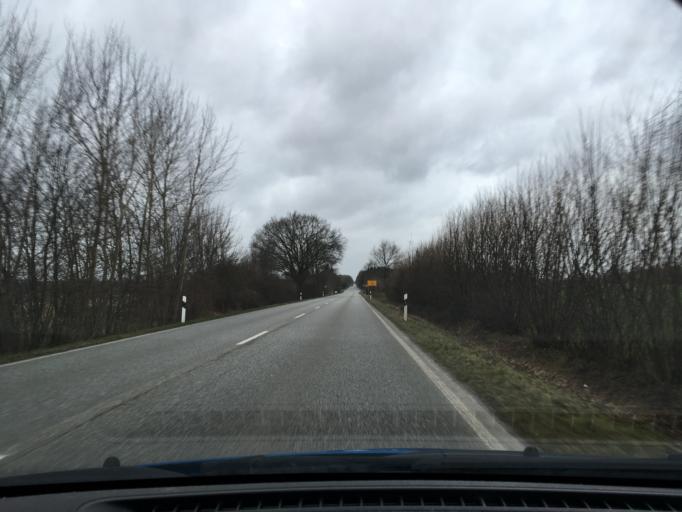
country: DE
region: Schleswig-Holstein
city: Wangelau
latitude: 53.4511
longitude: 10.5542
